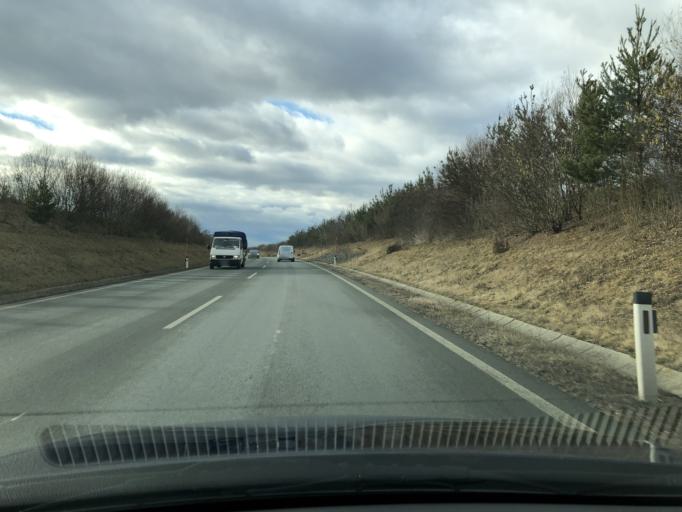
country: AT
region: Burgenland
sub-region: Politischer Bezirk Oberwart
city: Markt Neuhodis
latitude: 47.2685
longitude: 16.3799
